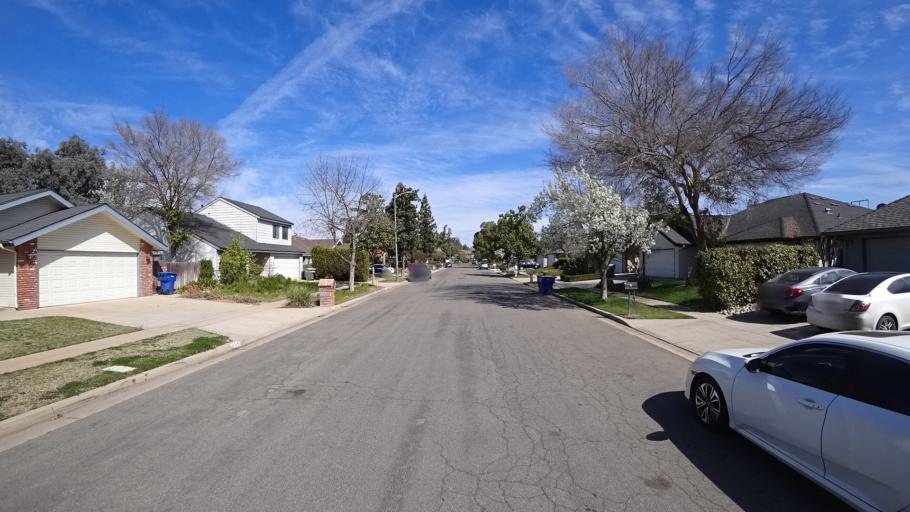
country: US
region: California
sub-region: Fresno County
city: Clovis
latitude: 36.8561
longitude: -119.7798
